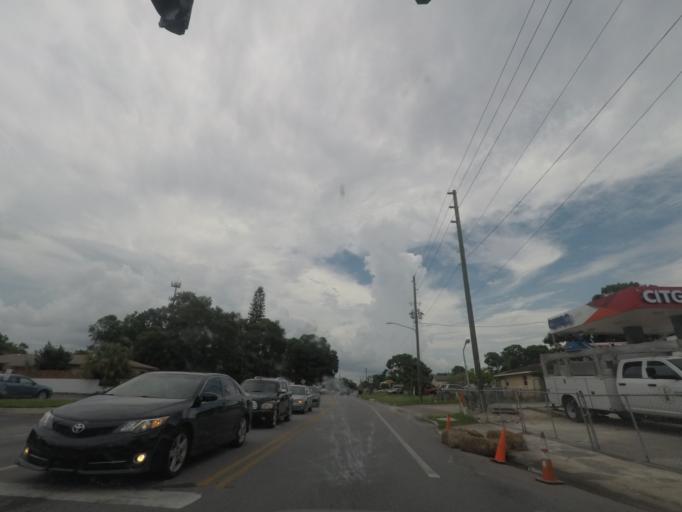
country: US
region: Florida
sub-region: Pinellas County
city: Lealman
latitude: 27.7992
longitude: -82.6712
